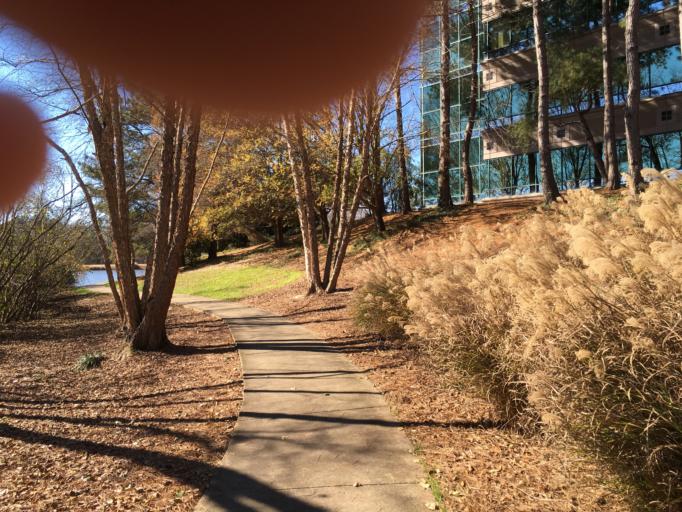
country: US
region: Georgia
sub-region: Fulton County
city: Johns Creek
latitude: 34.0624
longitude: -84.1689
